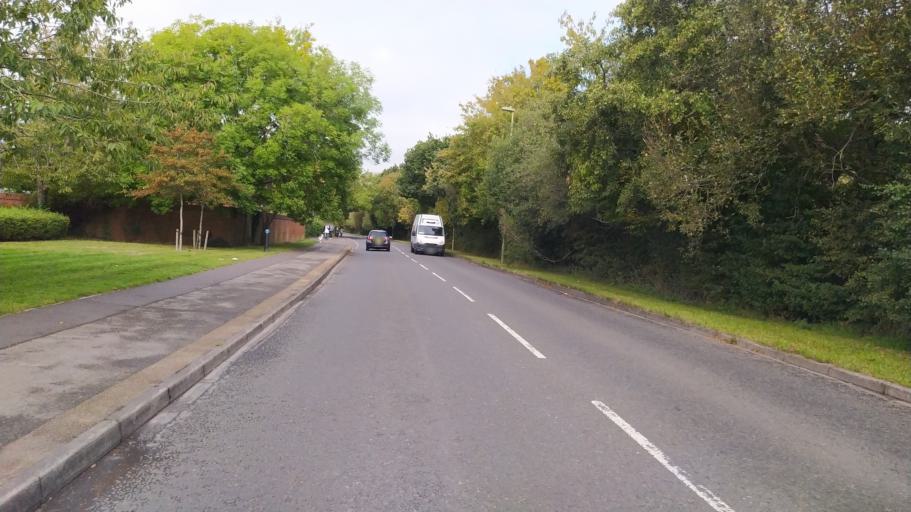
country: GB
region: England
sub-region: Hampshire
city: Lymington
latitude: 50.7666
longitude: -1.5443
